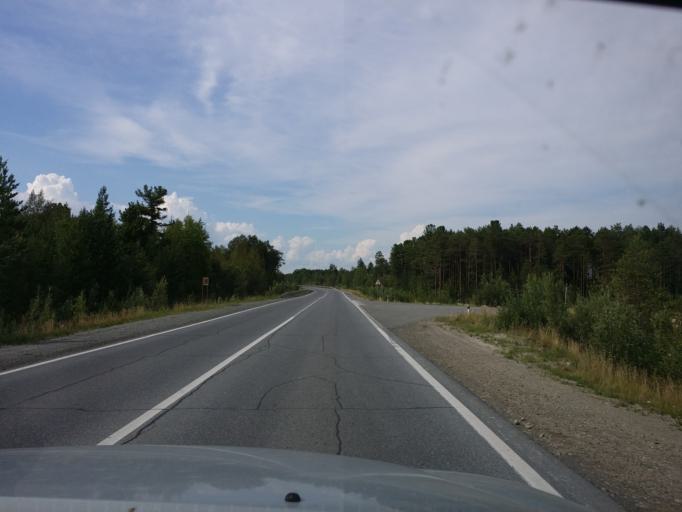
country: RU
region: Khanty-Mansiyskiy Avtonomnyy Okrug
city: Megion
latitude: 61.1149
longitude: 75.8410
